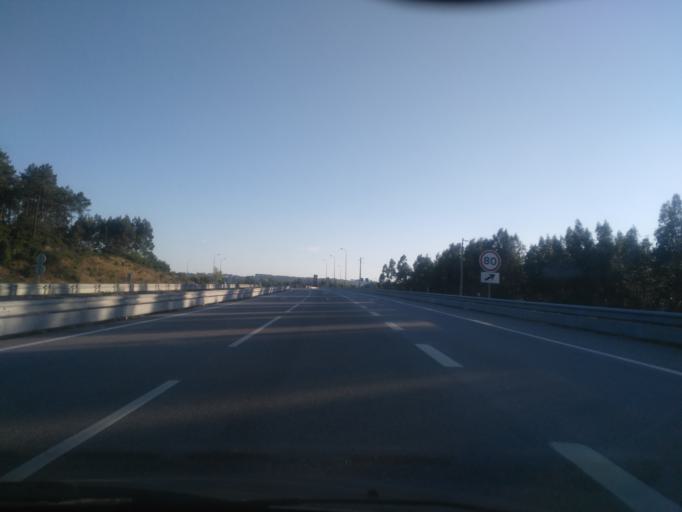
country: PT
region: Coimbra
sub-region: Figueira da Foz
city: Alhadas
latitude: 40.2157
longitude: -8.8079
